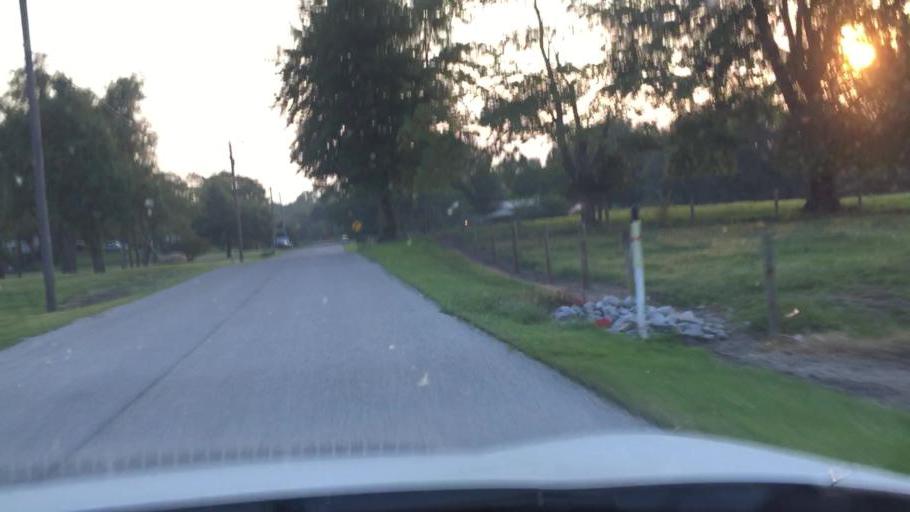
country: US
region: Ohio
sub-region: Clark County
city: Lisbon
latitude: 39.9449
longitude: -83.5861
